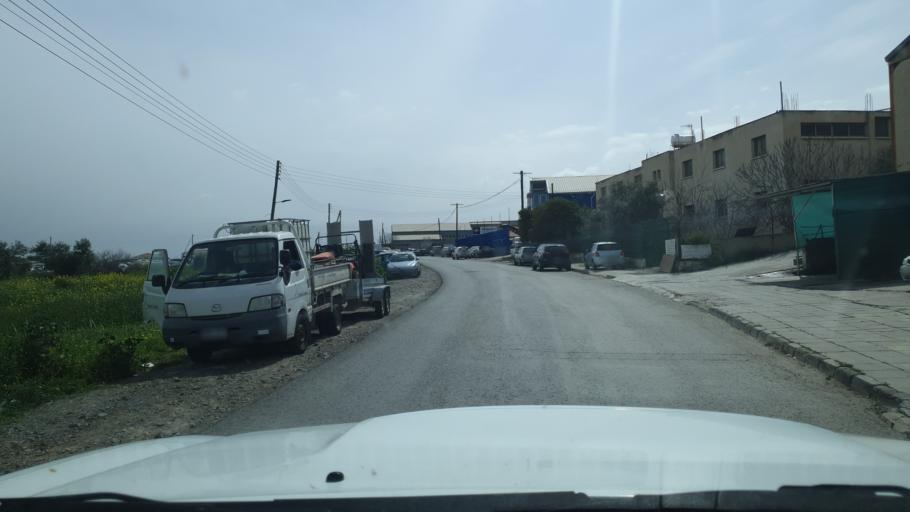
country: CY
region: Lefkosia
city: Geri
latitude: 35.0924
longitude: 33.3824
